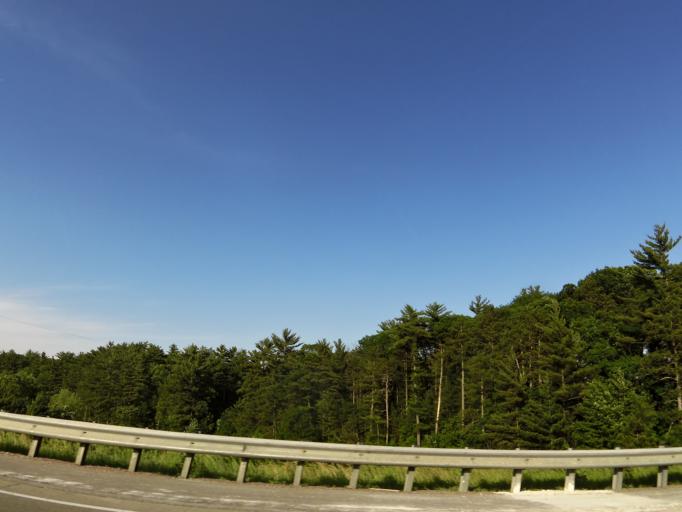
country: US
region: Wisconsin
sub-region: Sauk County
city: Lake Delton
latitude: 43.6329
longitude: -89.8077
